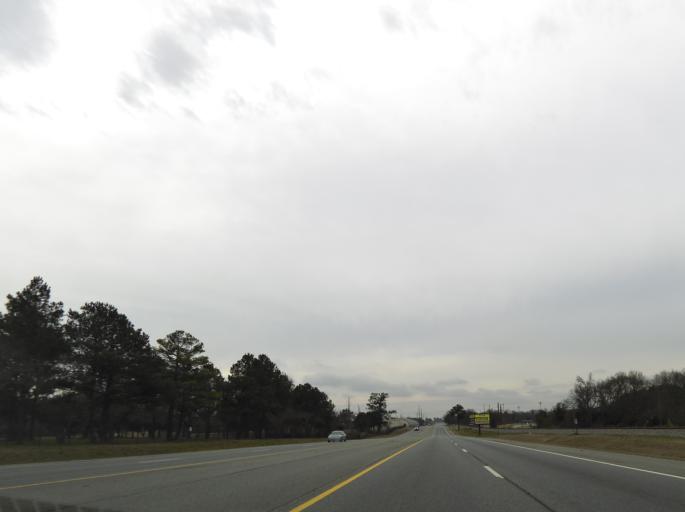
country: US
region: Georgia
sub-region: Houston County
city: Robins Air Force Base
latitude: 32.6092
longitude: -83.5961
